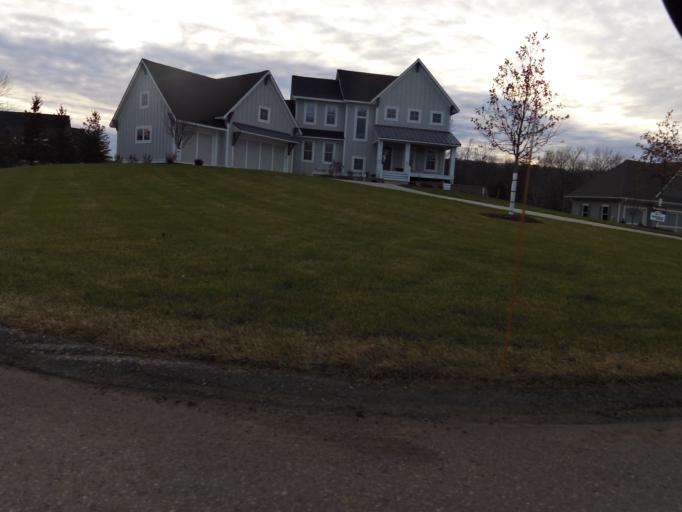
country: US
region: Minnesota
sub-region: Washington County
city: Bayport
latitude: 45.0007
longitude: -92.8002
